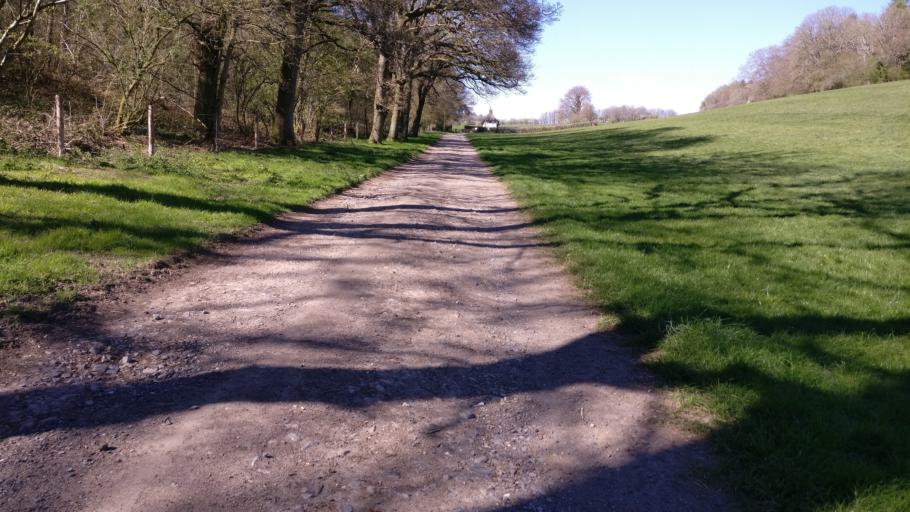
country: GB
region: England
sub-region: Hampshire
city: Basingstoke
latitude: 51.2101
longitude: -1.1051
